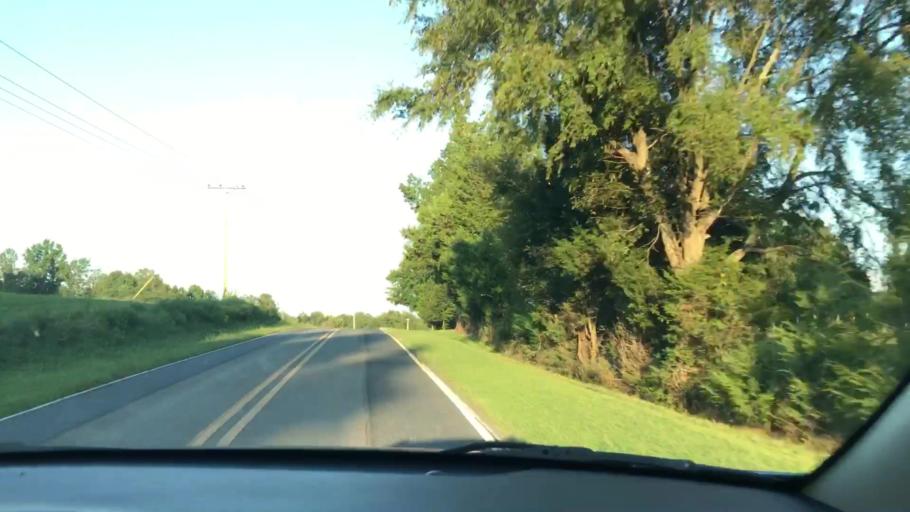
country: US
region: North Carolina
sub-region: Randolph County
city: Franklinville
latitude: 35.8009
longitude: -79.6777
